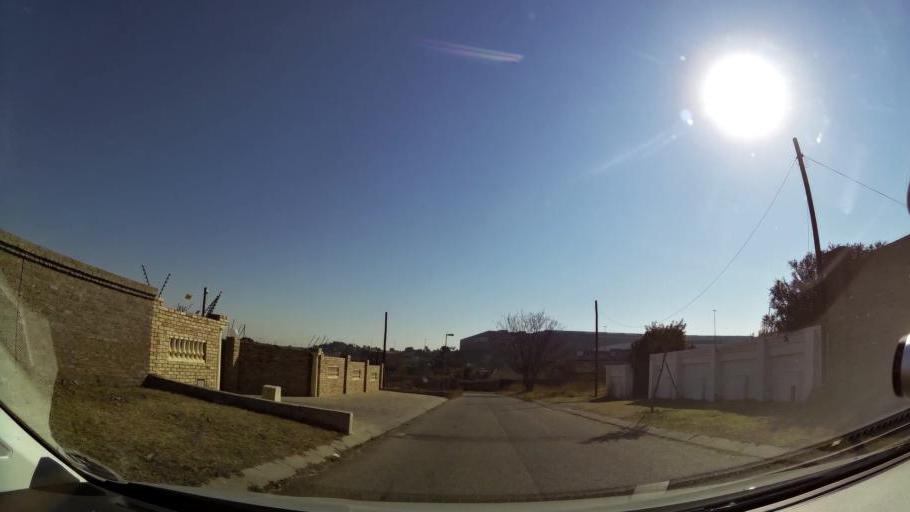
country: ZA
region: Gauteng
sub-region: City of Johannesburg Metropolitan Municipality
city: Modderfontein
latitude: -26.1114
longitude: 28.1290
